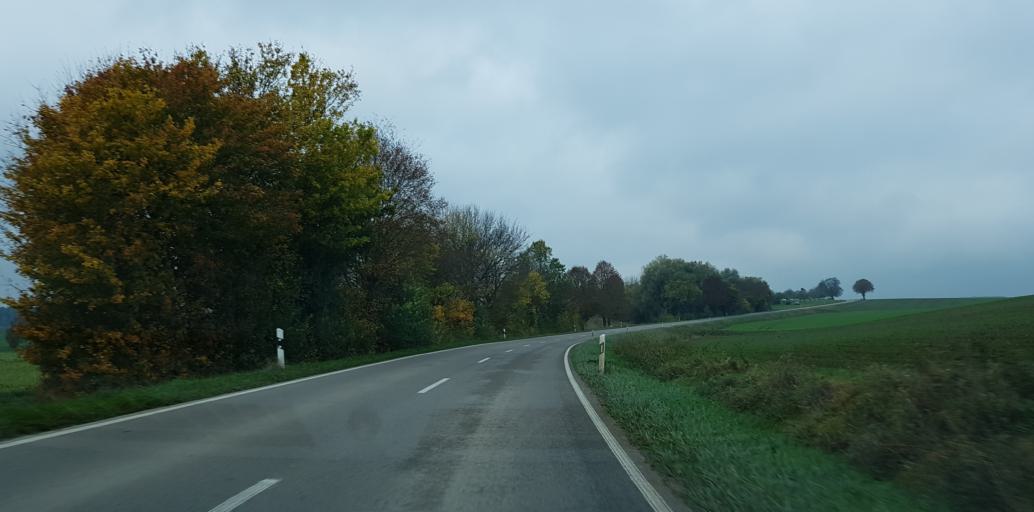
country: DE
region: Baden-Wuerttemberg
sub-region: Tuebingen Region
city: Oberdischingen
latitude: 48.3033
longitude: 9.8184
